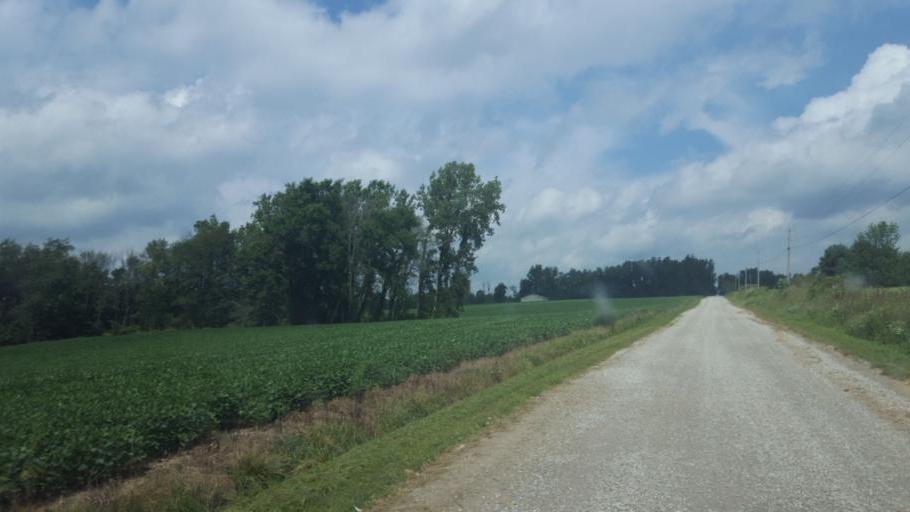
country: US
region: Ohio
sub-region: Richland County
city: Lexington
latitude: 40.6555
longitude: -82.6898
